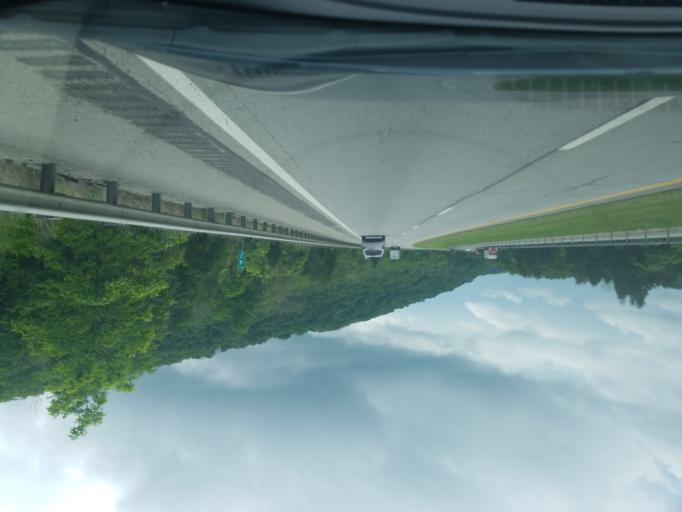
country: US
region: Kentucky
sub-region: Carroll County
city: Carrollton
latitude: 38.6256
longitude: -85.1527
